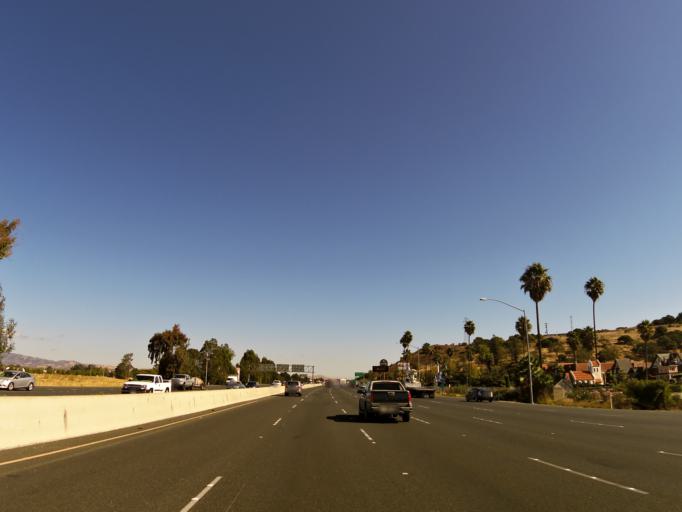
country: US
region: California
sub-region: Solano County
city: Green Valley
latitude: 38.2246
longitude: -122.1261
